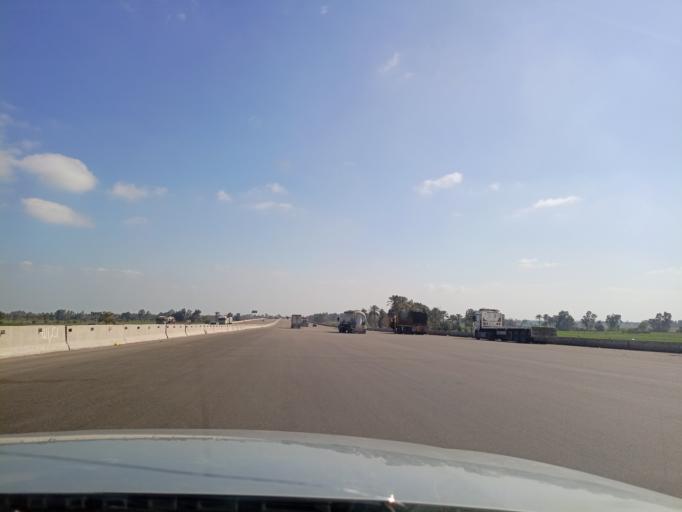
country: EG
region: Muhafazat al Qalyubiyah
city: Banha
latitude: 30.4660
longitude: 31.3005
